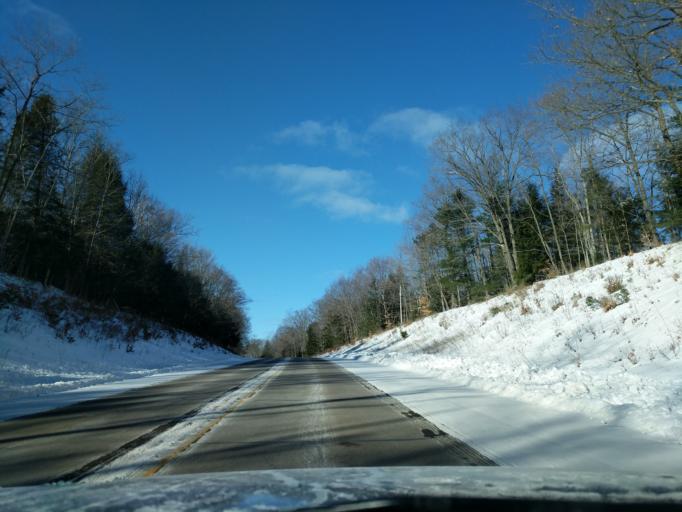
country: US
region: Wisconsin
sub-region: Menominee County
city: Keshena
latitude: 45.1463
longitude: -88.6829
